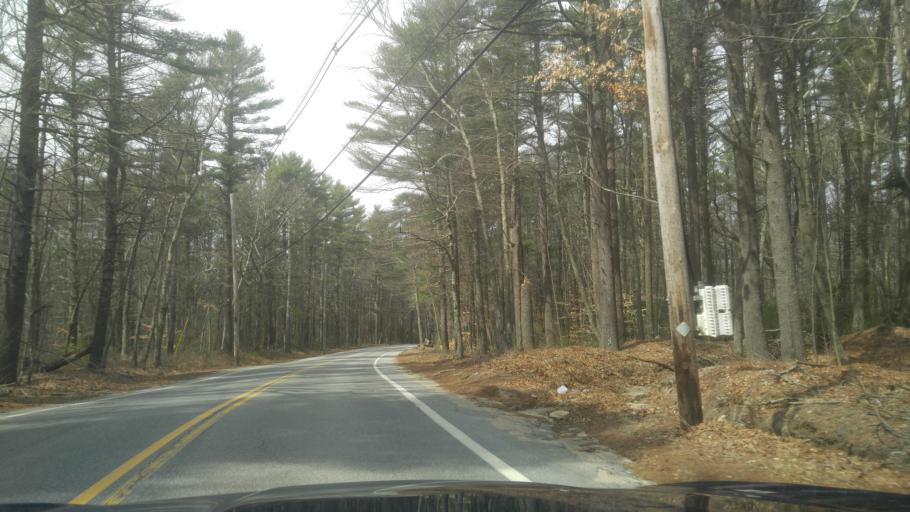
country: US
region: Rhode Island
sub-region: Washington County
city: Exeter
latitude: 41.6322
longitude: -71.5724
